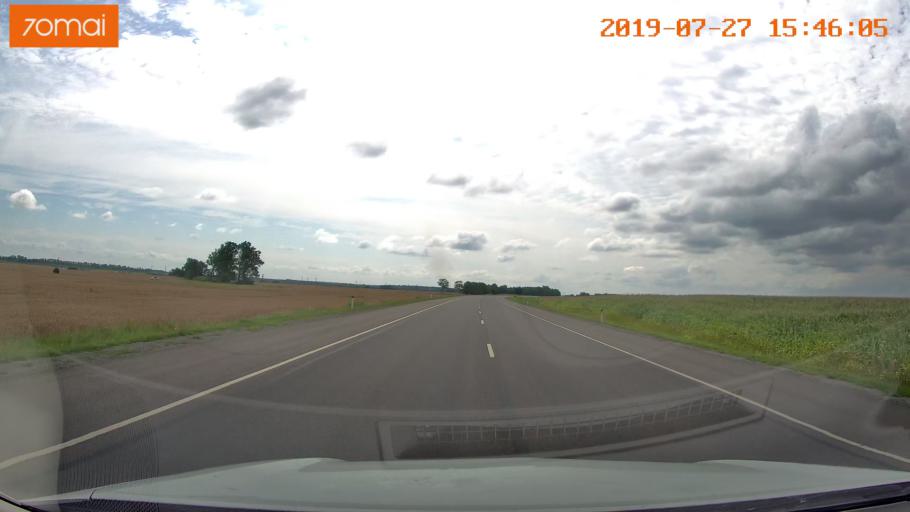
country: RU
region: Kaliningrad
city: Gusev
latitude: 54.6061
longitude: 22.1232
